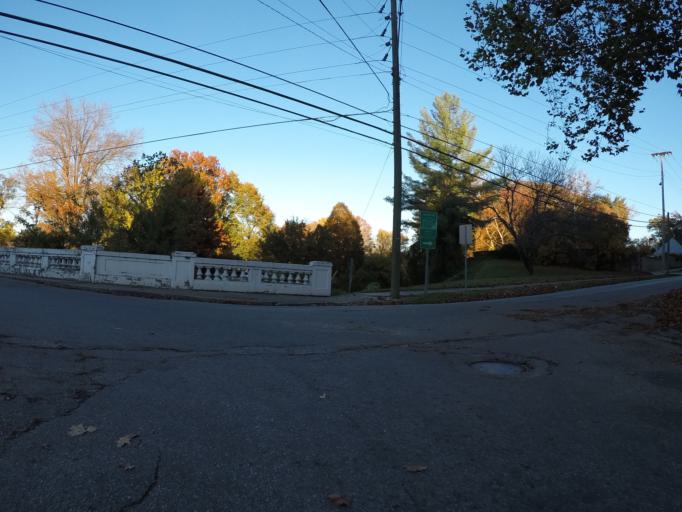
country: US
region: West Virginia
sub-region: Cabell County
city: Huntington
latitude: 38.4066
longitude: -82.4417
